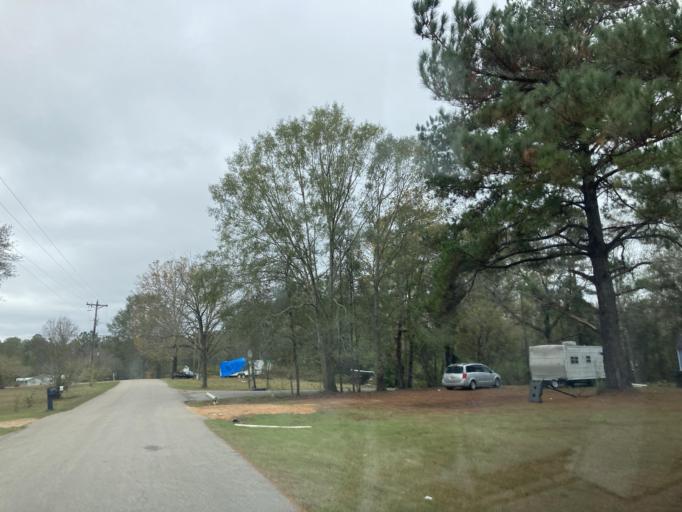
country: US
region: Mississippi
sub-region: Lamar County
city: West Hattiesburg
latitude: 31.2557
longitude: -89.4938
